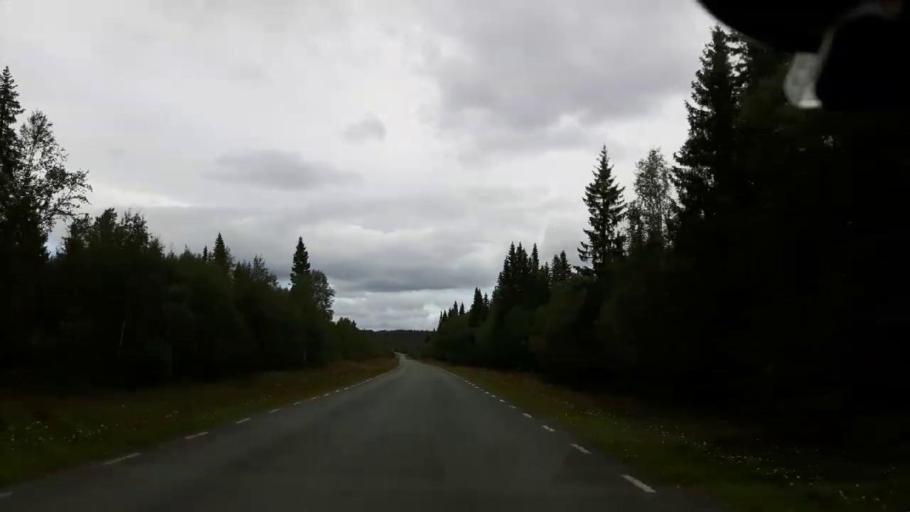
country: SE
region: Jaemtland
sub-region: Krokoms Kommun
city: Valla
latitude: 63.5607
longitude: 13.8480
